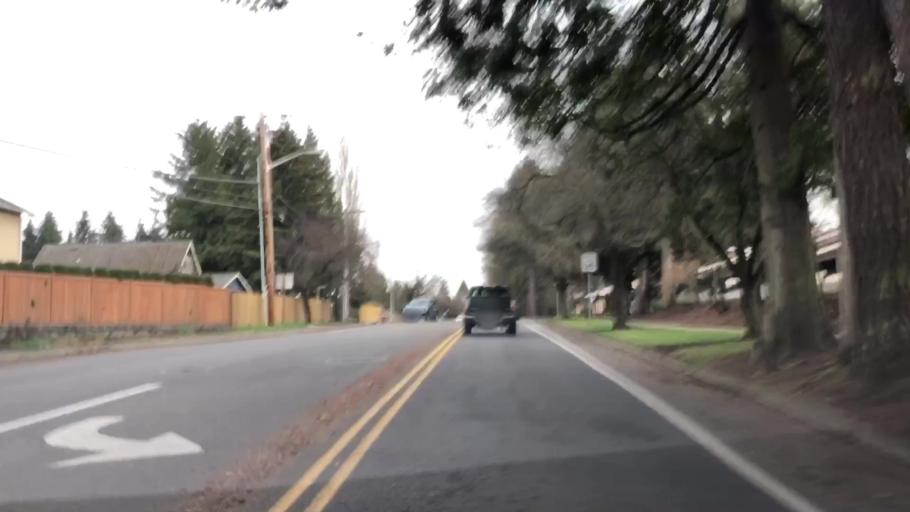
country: US
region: Washington
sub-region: King County
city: Kingsgate
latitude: 47.7186
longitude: -122.1748
